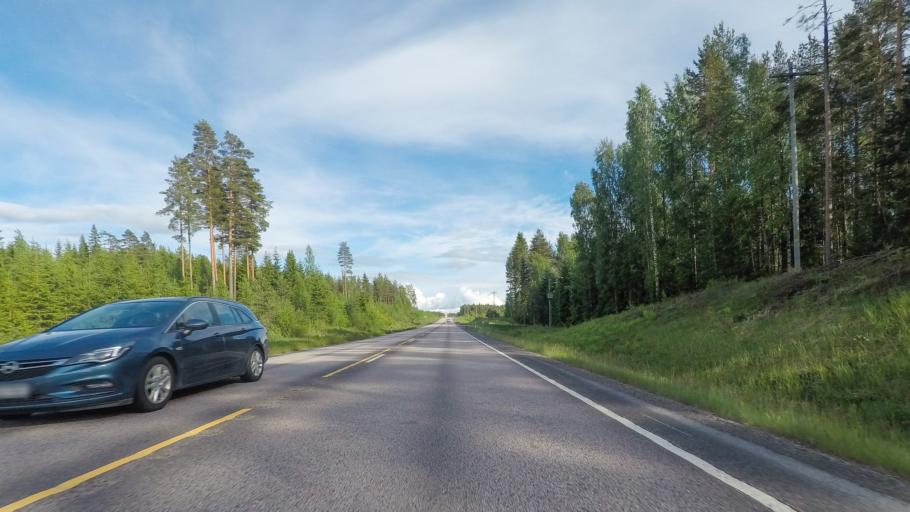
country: FI
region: Central Finland
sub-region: Joutsa
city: Leivonmaeki
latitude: 61.9624
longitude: 26.0903
